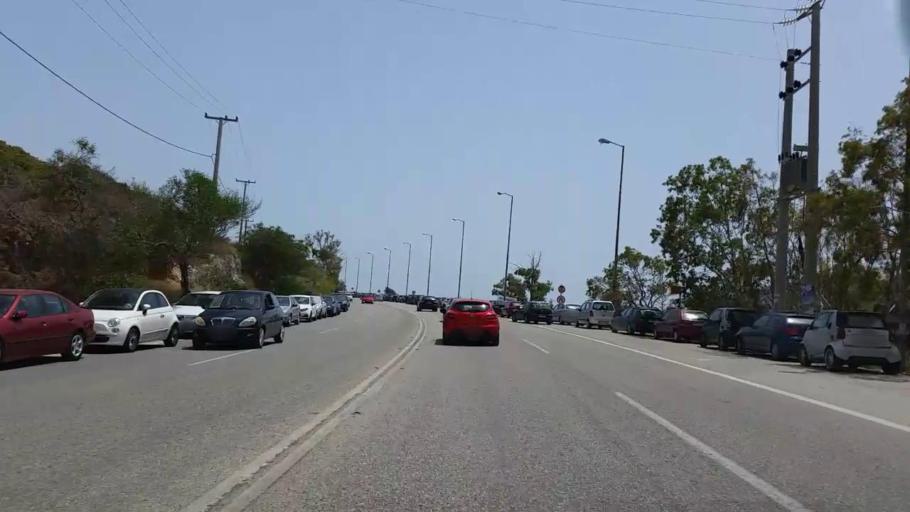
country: GR
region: Attica
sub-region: Nomarchia Anatolikis Attikis
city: Saronida
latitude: 37.7246
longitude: 23.9082
